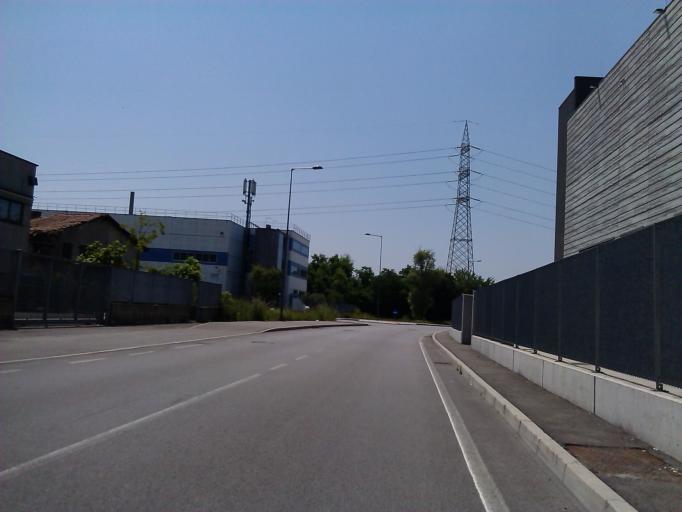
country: IT
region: Veneto
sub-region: Provincia di Venezia
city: Mestre
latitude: 45.4584
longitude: 12.2140
